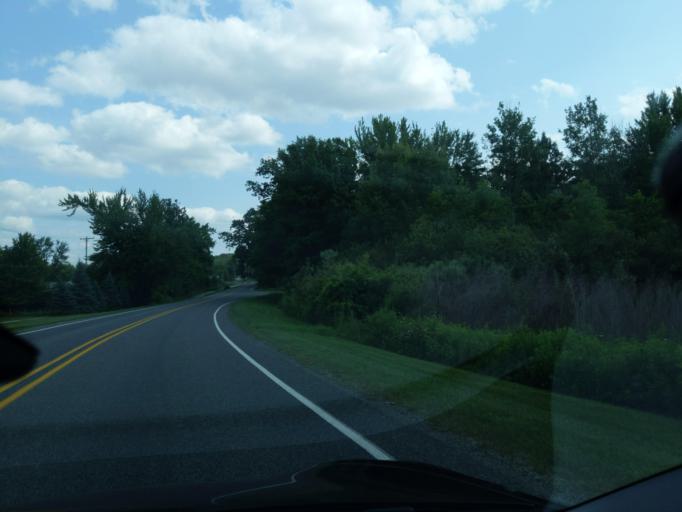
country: US
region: Michigan
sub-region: Kent County
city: Forest Hills
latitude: 42.9794
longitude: -85.5348
